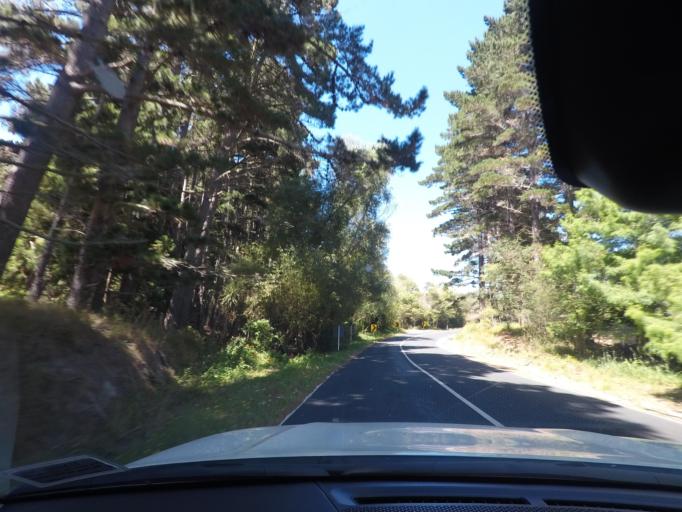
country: NZ
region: Auckland
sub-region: Auckland
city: Parakai
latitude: -36.5754
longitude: 174.3554
